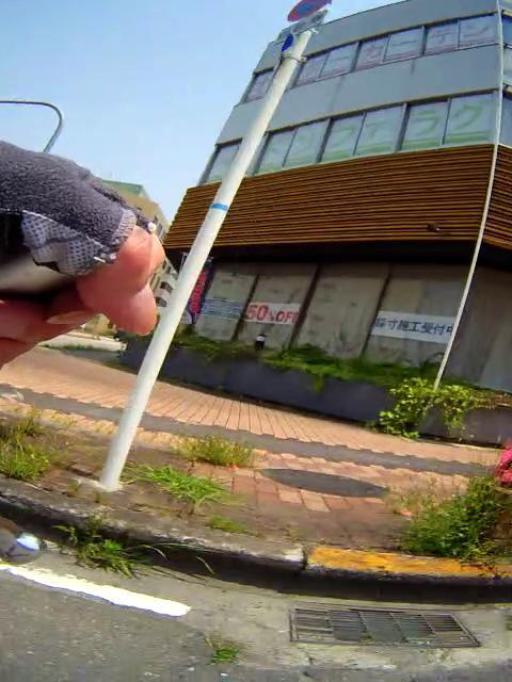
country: JP
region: Osaka
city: Mino
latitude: 34.8212
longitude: 135.4904
